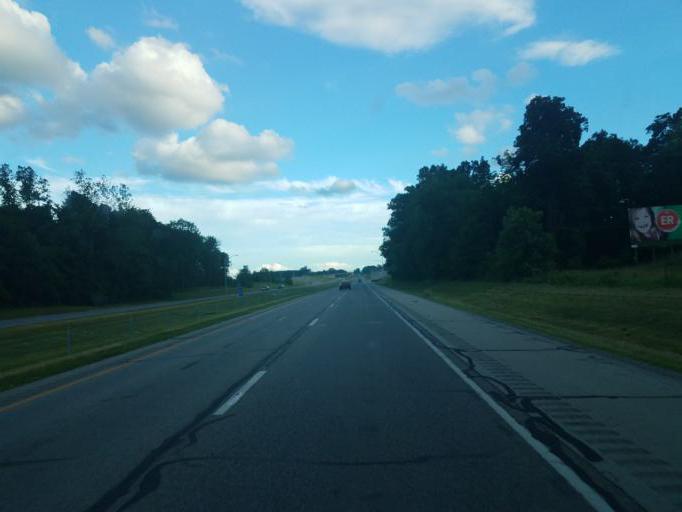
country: US
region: Indiana
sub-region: Allen County
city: Huntertown
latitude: 41.2080
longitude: -85.1047
